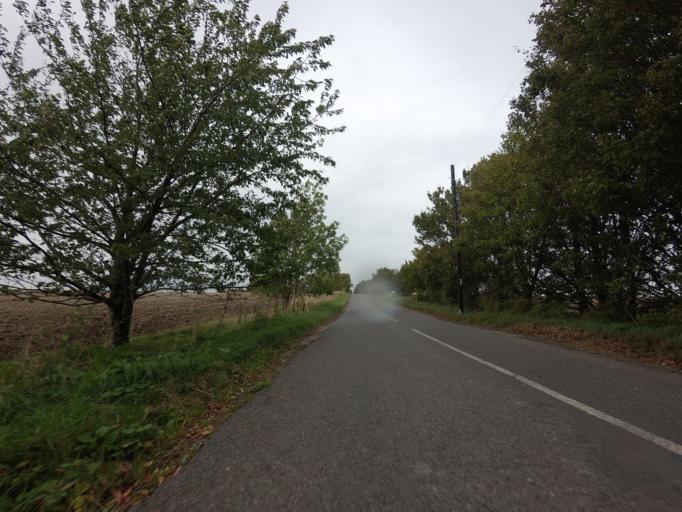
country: GB
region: England
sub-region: Cambridgeshire
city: Harston
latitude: 52.0818
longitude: 0.0807
